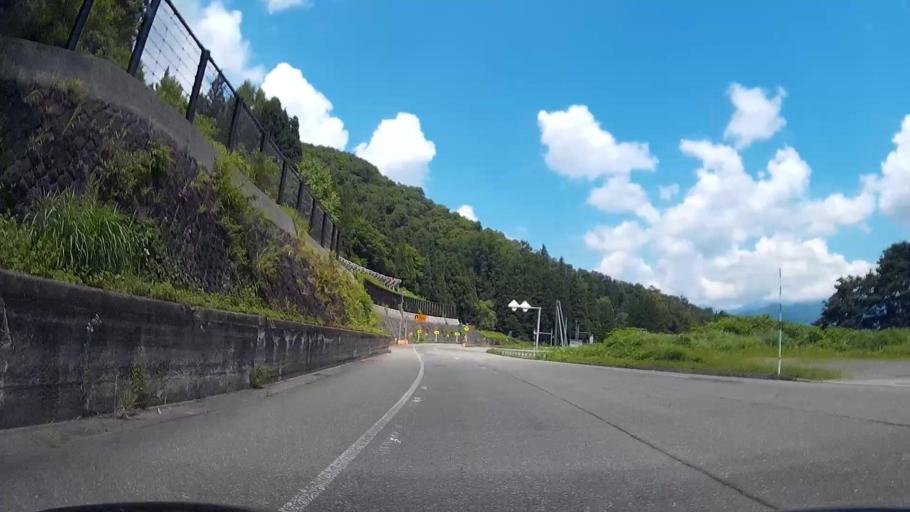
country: JP
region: Niigata
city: Shiozawa
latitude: 36.9130
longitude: 138.7960
